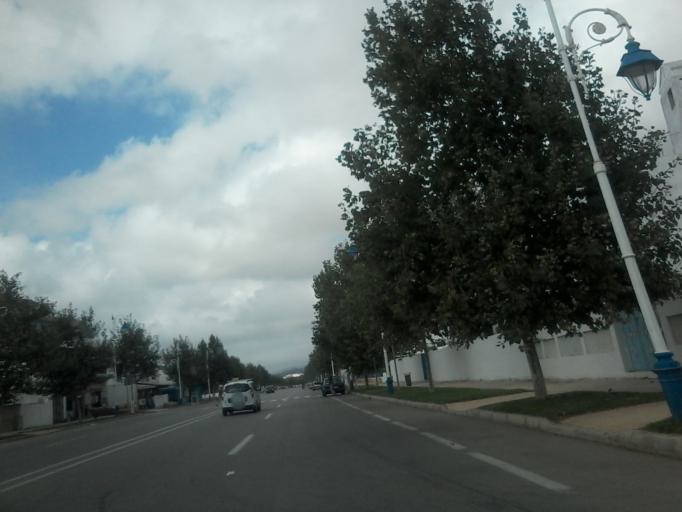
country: MA
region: Tanger-Tetouan
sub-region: Tetouan
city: Martil
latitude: 35.6370
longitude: -5.2891
